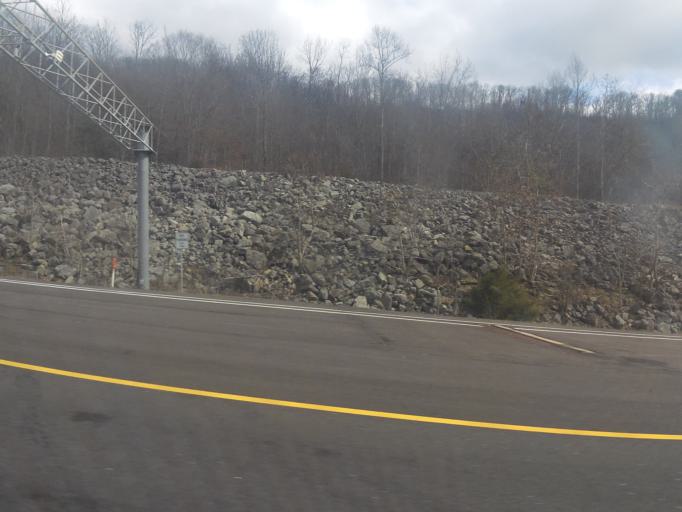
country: US
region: Tennessee
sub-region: Marion County
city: Monteagle
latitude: 35.1981
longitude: -85.8137
